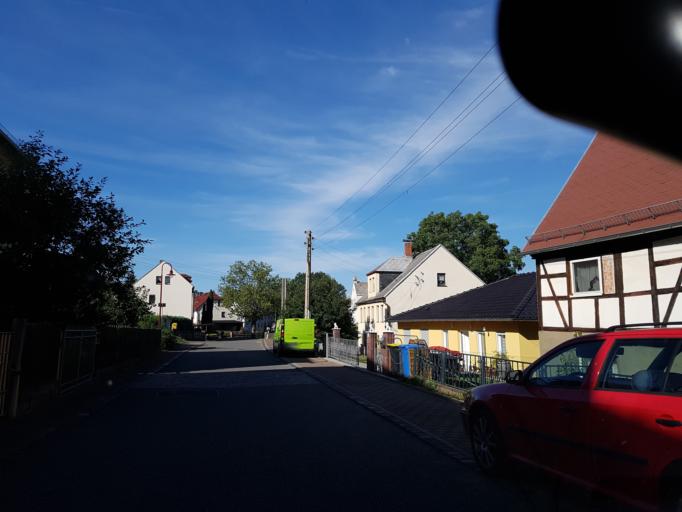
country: DE
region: Saxony
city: Waldheim
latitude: 51.0831
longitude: 13.0331
